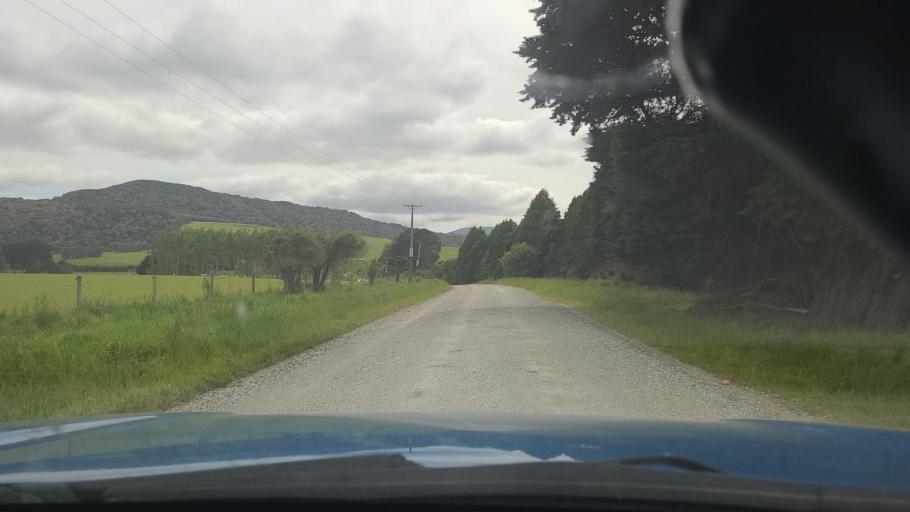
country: NZ
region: Otago
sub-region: Clutha District
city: Papatowai
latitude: -46.5271
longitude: 169.1316
